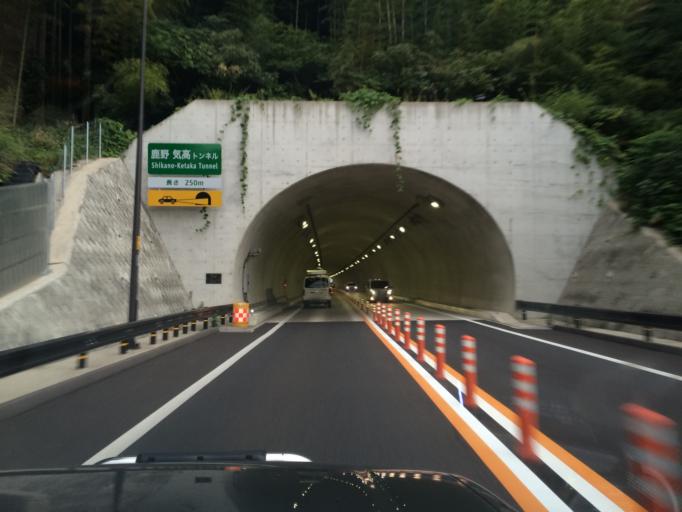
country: JP
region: Tottori
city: Tottori
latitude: 35.4984
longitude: 134.0430
